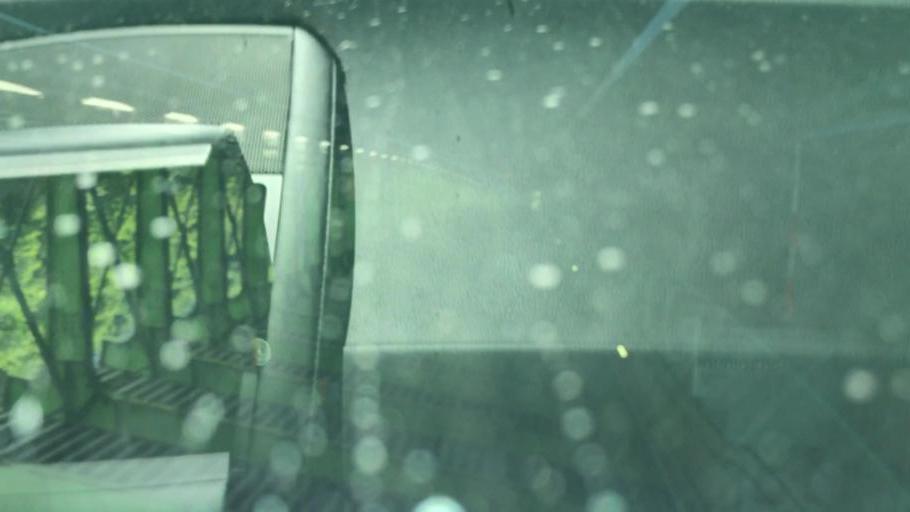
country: JP
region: Hokkaido
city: Shimo-furano
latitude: 42.9381
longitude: 142.5988
